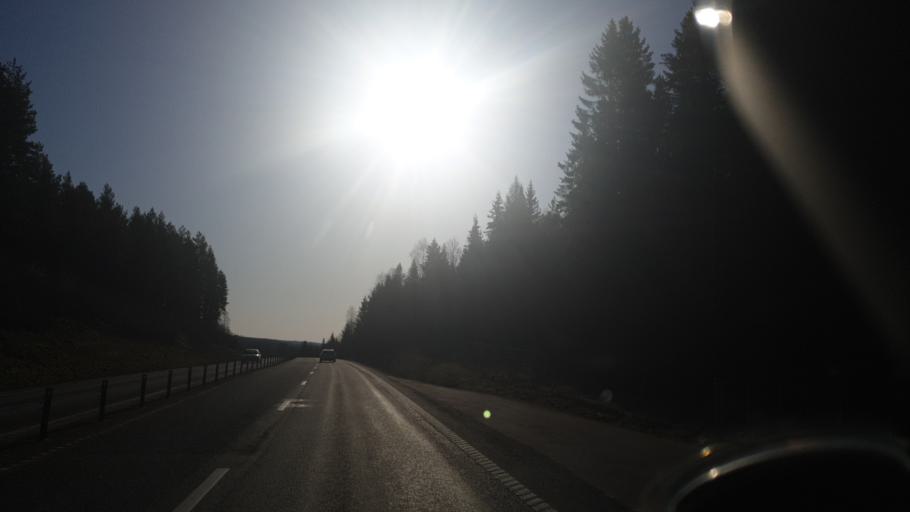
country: SE
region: Vaermland
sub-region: Arvika Kommun
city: Arvika
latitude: 59.6448
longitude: 12.7256
